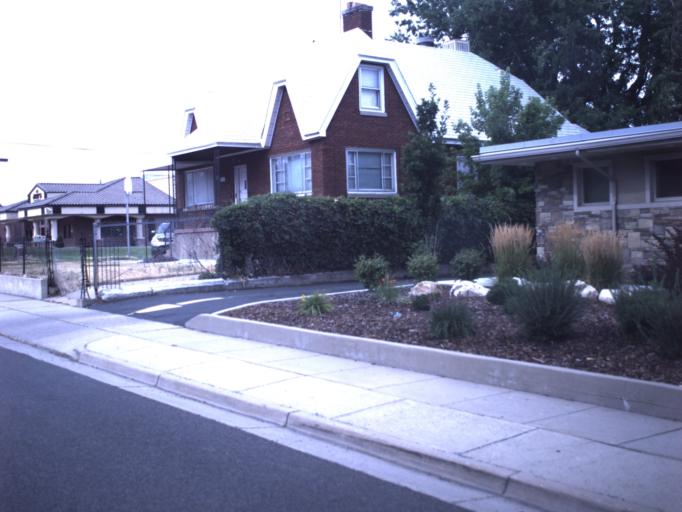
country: US
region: Utah
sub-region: Weber County
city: South Ogden
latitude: 41.2000
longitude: -111.9488
